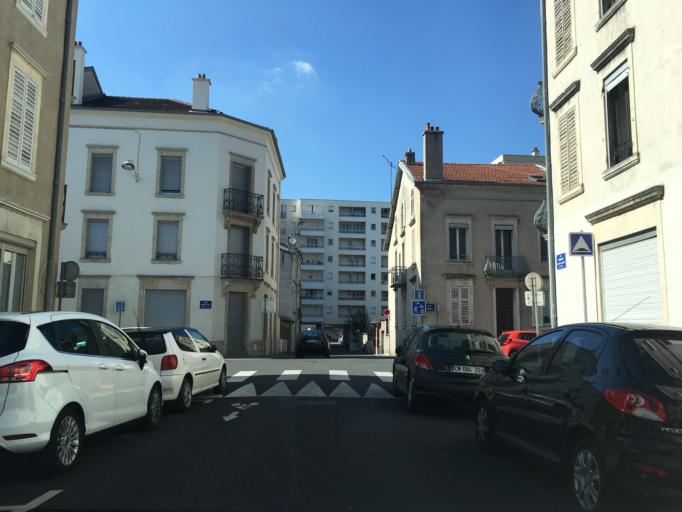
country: FR
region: Lorraine
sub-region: Departement de Meurthe-et-Moselle
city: Nancy
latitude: 48.6800
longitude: 6.1740
